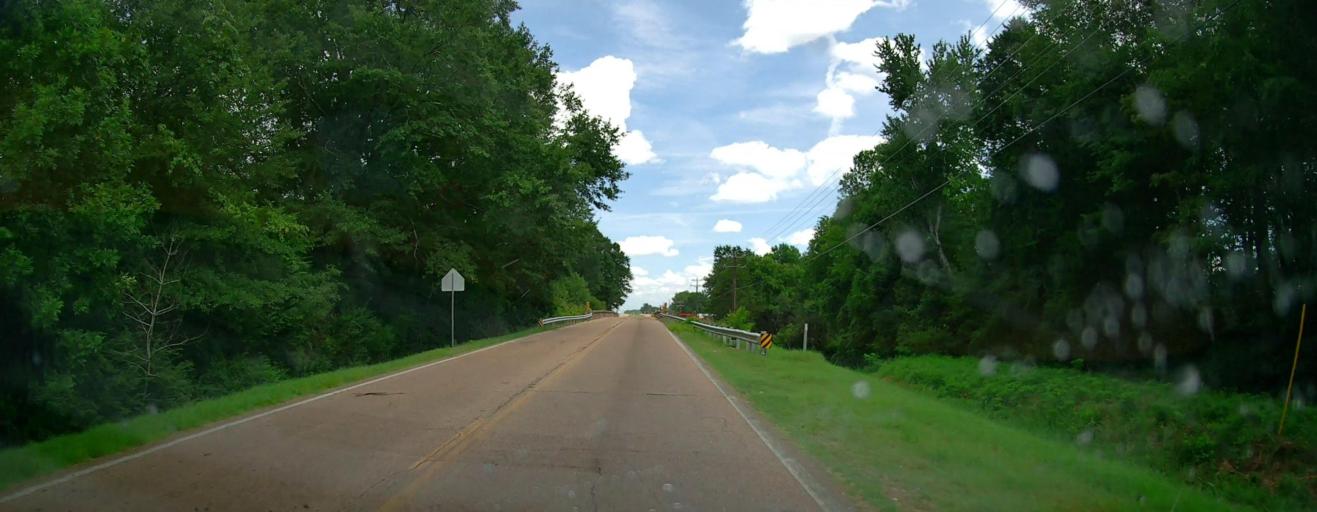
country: US
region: Mississippi
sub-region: Lee County
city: Shannon
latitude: 34.1214
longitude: -88.7124
